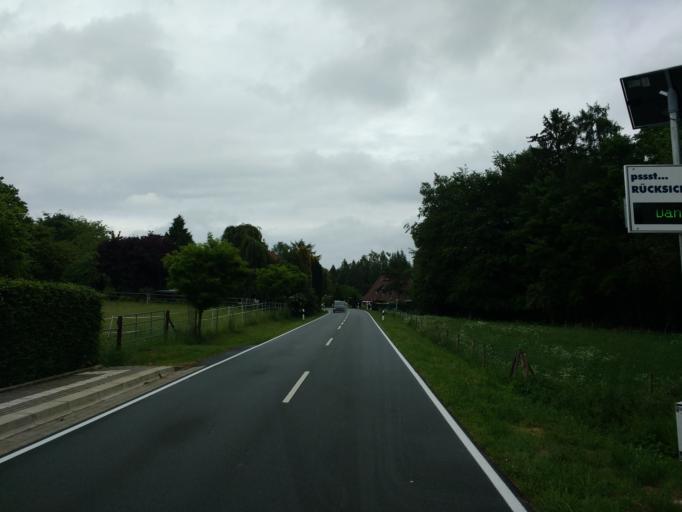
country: DE
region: Lower Saxony
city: Bad Iburg
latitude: 52.1741
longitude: 8.0715
